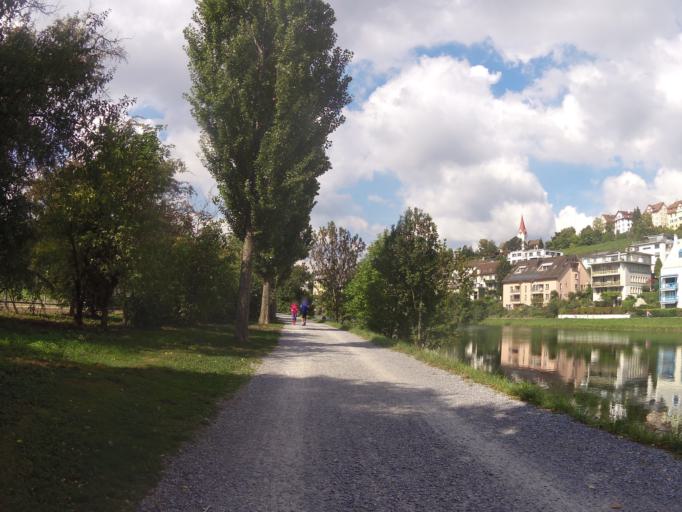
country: CH
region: Zurich
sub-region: Bezirk Zuerich
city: Zuerich (Kreis 10) / Hoengg
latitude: 47.3976
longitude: 8.4999
